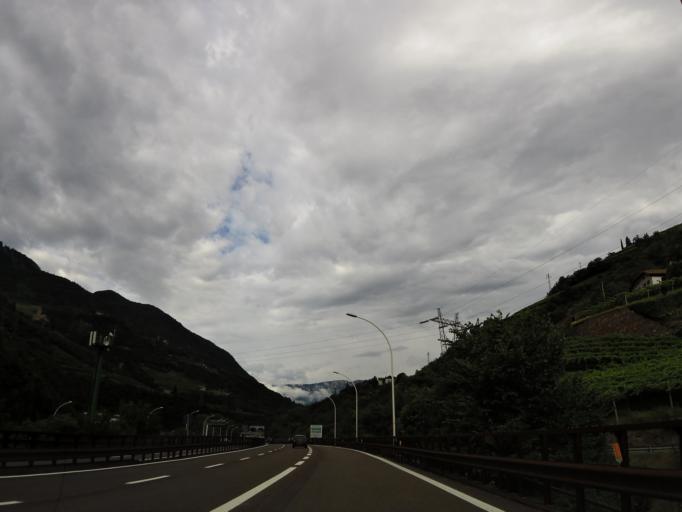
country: IT
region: Trentino-Alto Adige
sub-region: Bolzano
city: Cornedo All'Isarco
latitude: 46.4950
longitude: 11.4079
